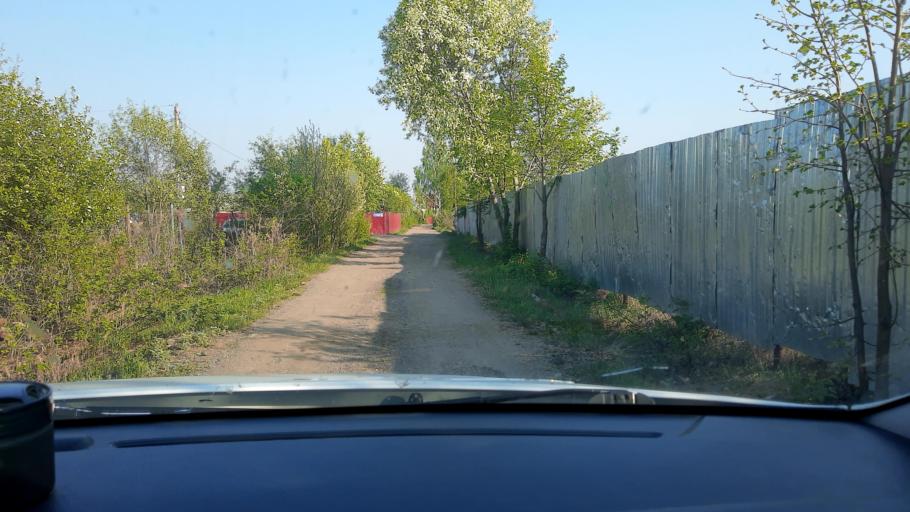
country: RU
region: Bashkortostan
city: Avdon
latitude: 54.5742
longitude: 55.8789
